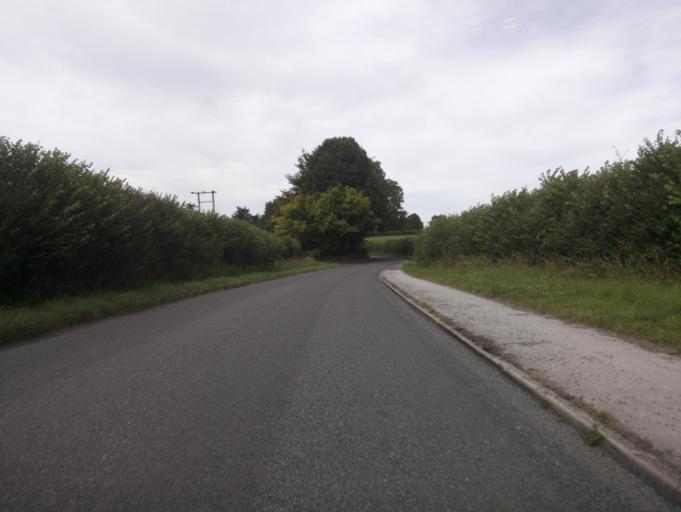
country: GB
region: England
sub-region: Somerset
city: Ilchester
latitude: 51.0540
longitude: -2.6695
